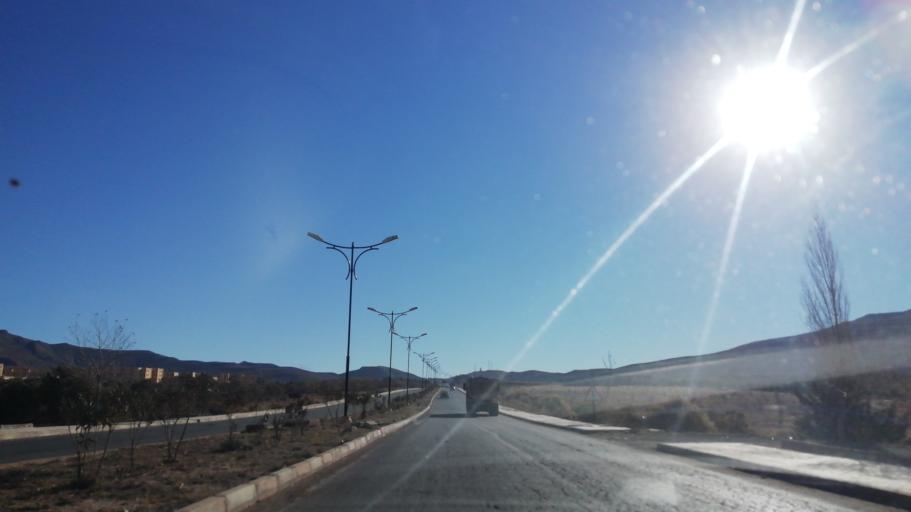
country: DZ
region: El Bayadh
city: El Bayadh
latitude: 33.6594
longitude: 1.0619
